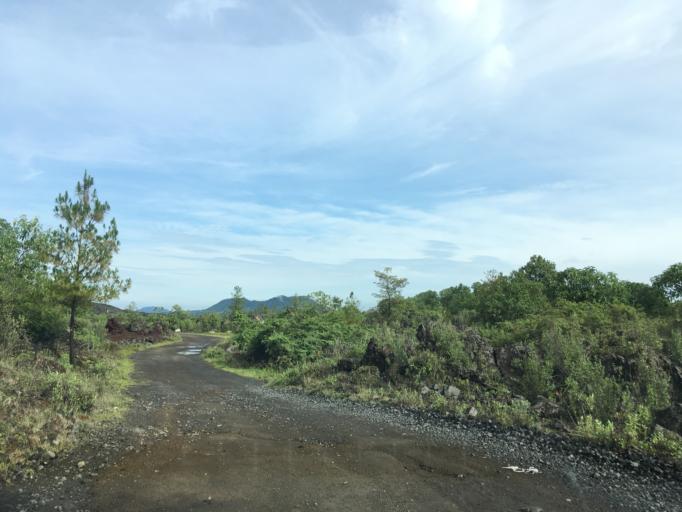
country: MX
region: Michoacan
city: Angahuan
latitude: 19.5196
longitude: -102.2230
